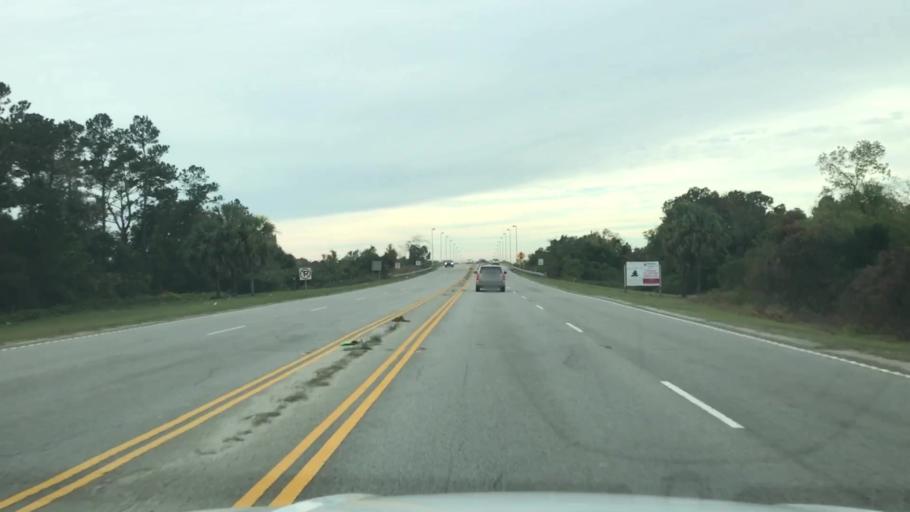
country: US
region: South Carolina
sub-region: Georgetown County
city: Georgetown
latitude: 33.3665
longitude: -79.2614
